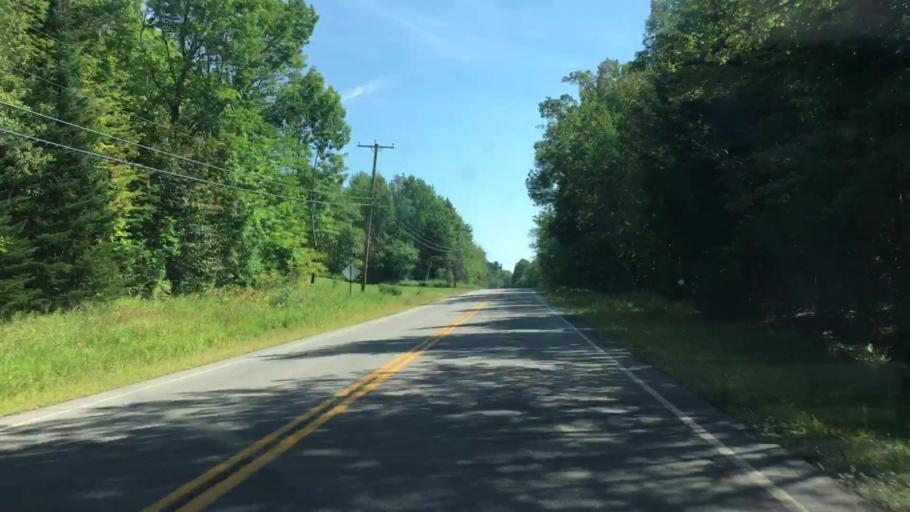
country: US
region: Maine
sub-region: Piscataquis County
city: Milo
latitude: 45.1980
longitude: -68.9047
